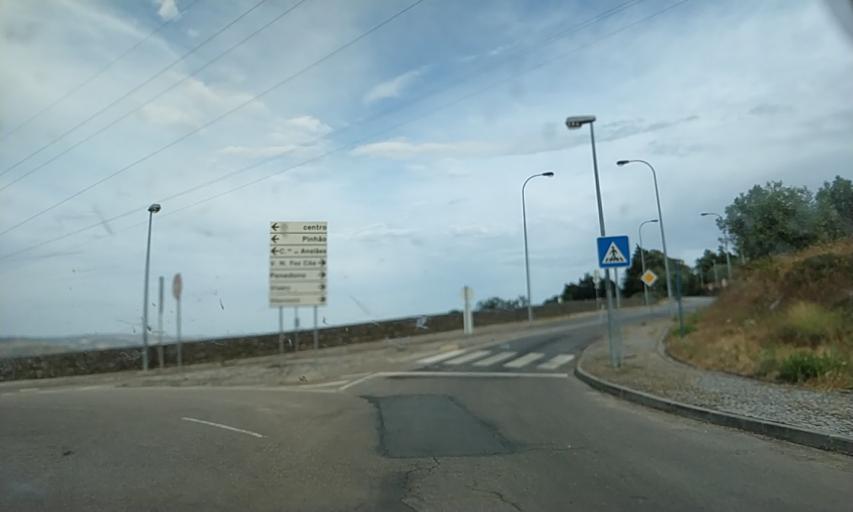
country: PT
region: Viseu
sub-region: Sao Joao da Pesqueira
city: Sao Joao da Pesqueira
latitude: 41.1431
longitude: -7.4021
